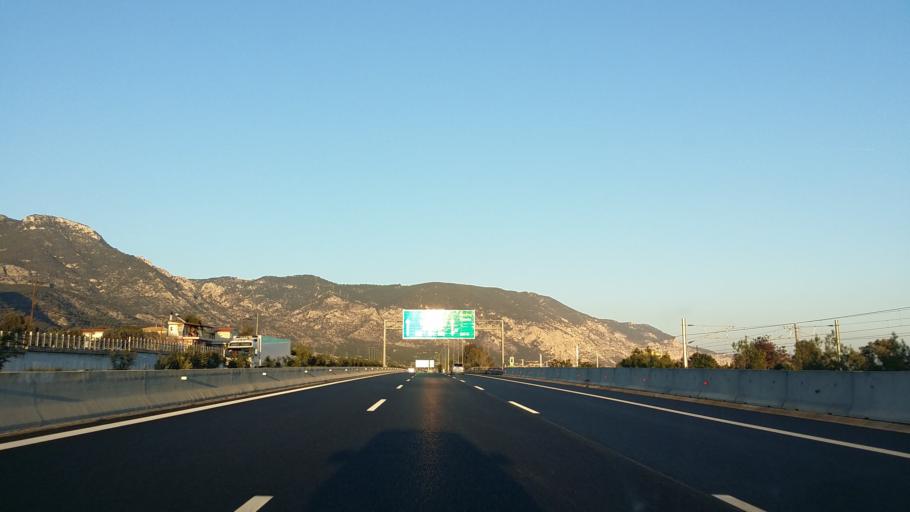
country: GR
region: Attica
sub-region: Nomarchia Dytikis Attikis
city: Kineta
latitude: 37.9603
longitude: 23.1902
